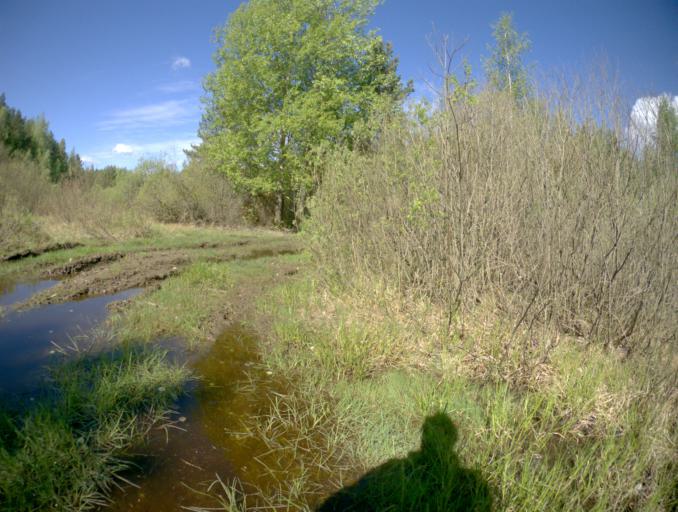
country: RU
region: Rjazan
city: Spas-Klepiki
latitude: 55.2489
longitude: 40.0940
